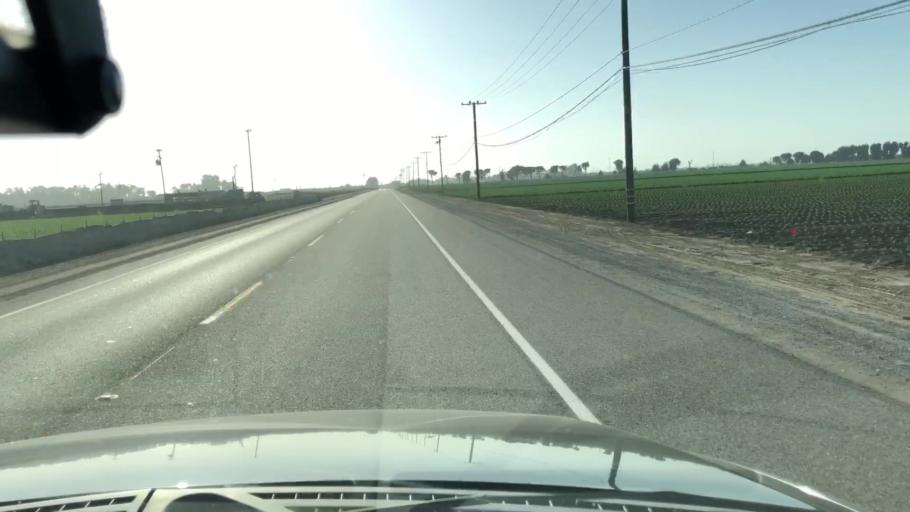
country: US
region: California
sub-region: Ventura County
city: Oxnard Shores
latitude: 34.2195
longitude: -119.2317
